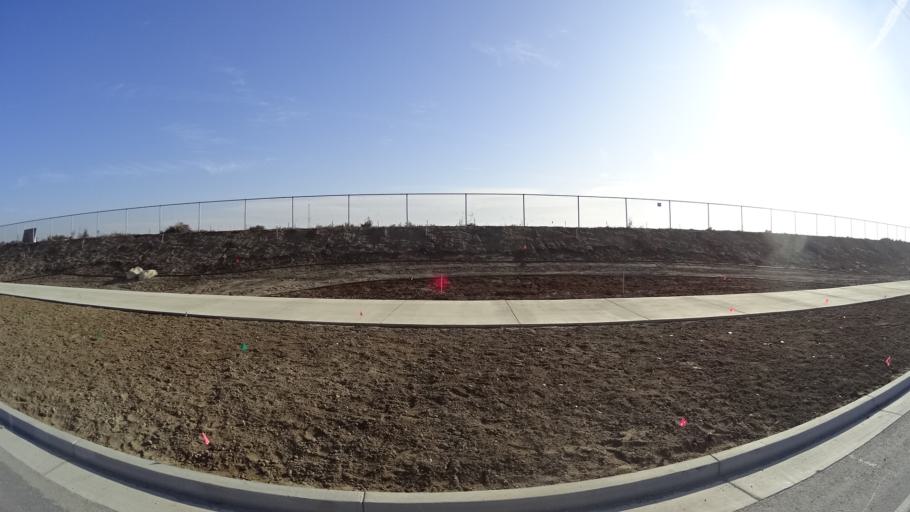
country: US
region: California
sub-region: Kern County
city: Greenfield
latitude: 35.2784
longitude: -119.0920
